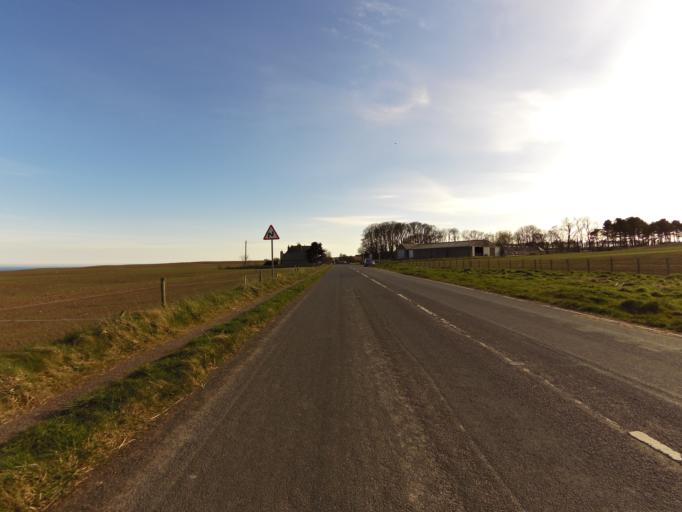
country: GB
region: Scotland
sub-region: Aberdeenshire
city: Stonehaven
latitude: 56.9468
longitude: -2.2055
